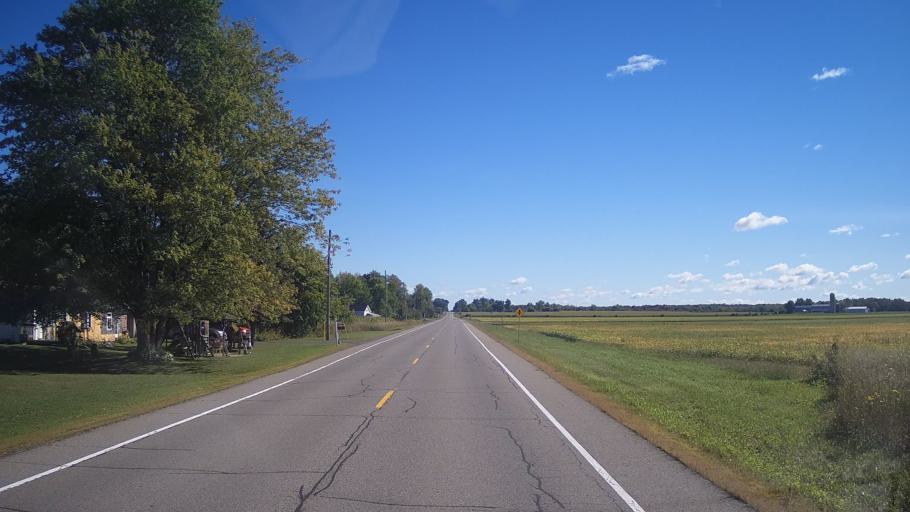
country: US
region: New York
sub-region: St. Lawrence County
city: Ogdensburg
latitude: 44.9334
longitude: -75.3240
